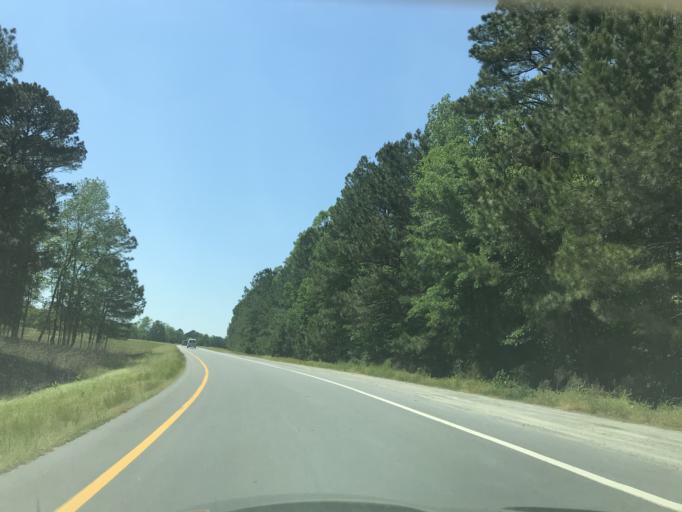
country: US
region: North Carolina
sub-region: Johnston County
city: Benson
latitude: 35.3306
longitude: -78.4490
